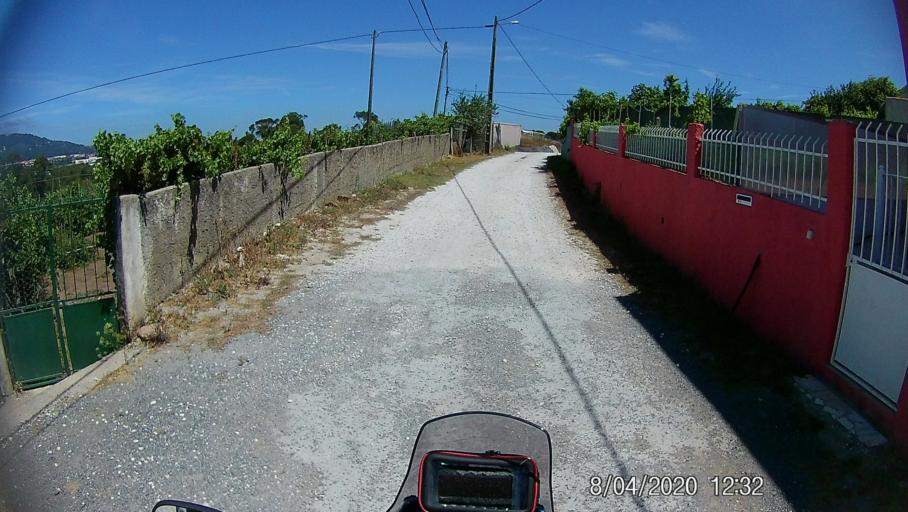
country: PT
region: Lisbon
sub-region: Sintra
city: Rio de Mouro
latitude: 38.7524
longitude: -9.3636
